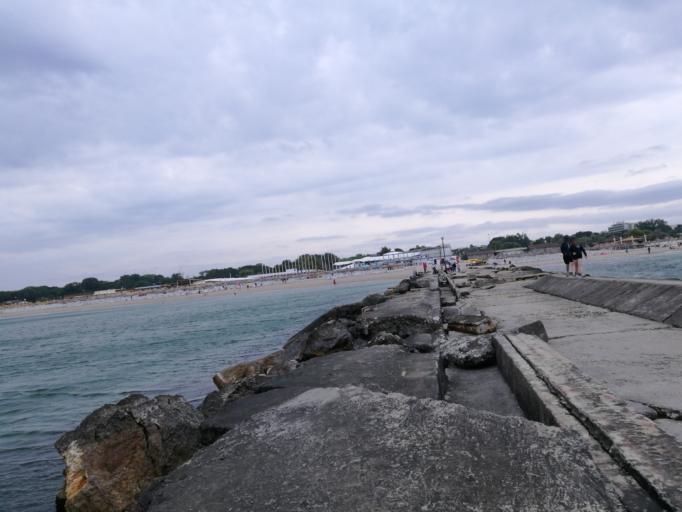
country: RO
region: Constanta
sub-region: Comuna Douazeci si Trei August
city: Douazeci si Trei August
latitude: 43.8669
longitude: 28.6081
